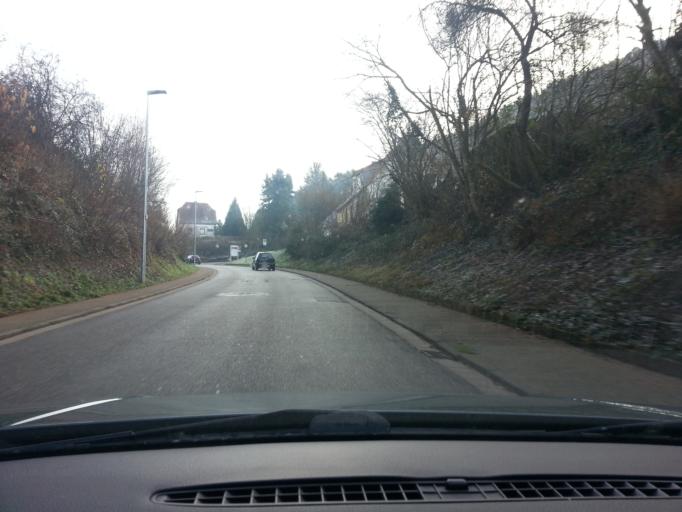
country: DE
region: Rheinland-Pfalz
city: Hauenstein
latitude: 49.1897
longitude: 7.8588
